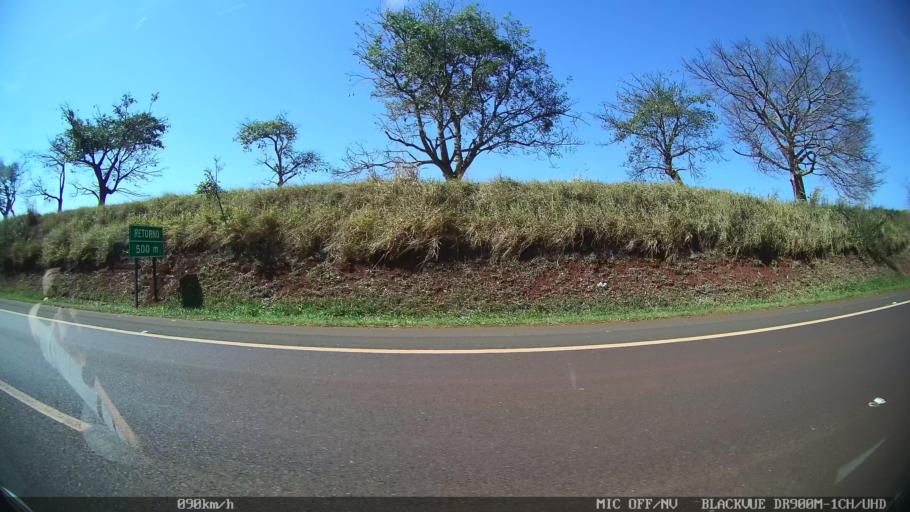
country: BR
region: Sao Paulo
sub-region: Batatais
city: Batatais
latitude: -20.7609
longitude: -47.5325
